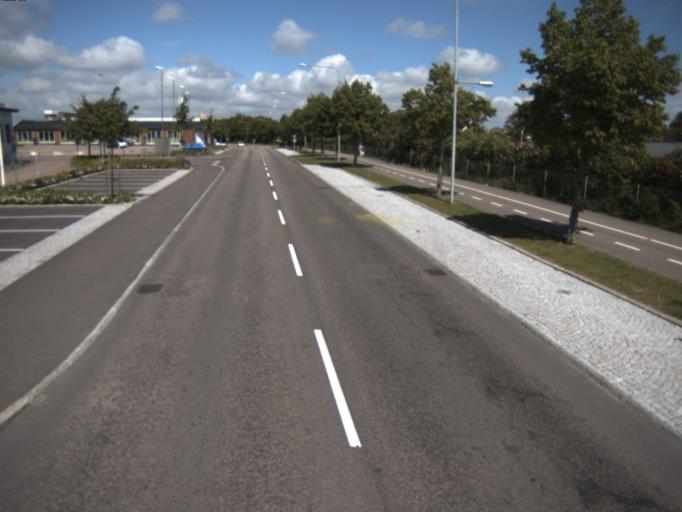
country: SE
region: Skane
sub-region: Helsingborg
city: Helsingborg
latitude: 56.0595
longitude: 12.7086
